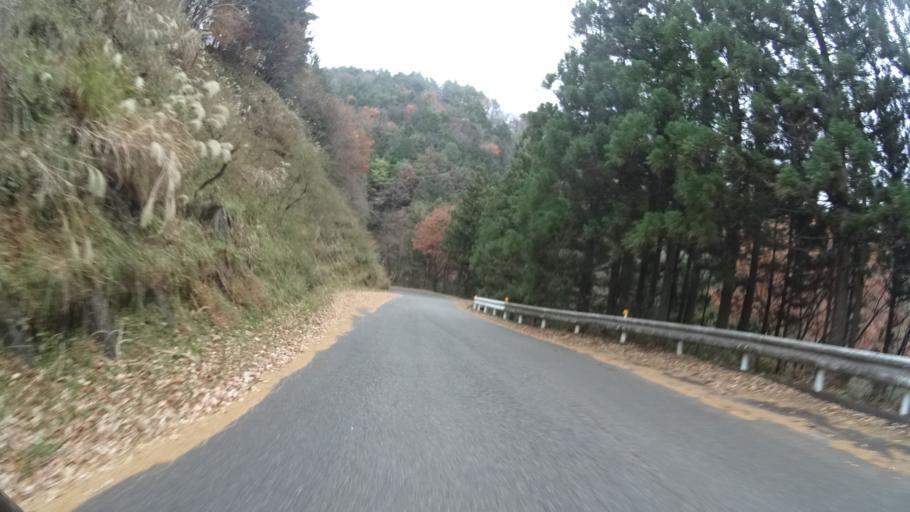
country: JP
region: Gunma
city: Omamacho-omama
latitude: 36.4985
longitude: 139.1827
